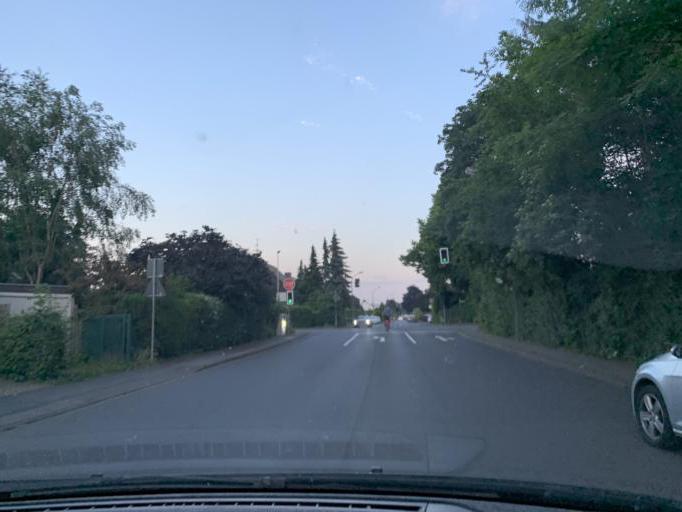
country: DE
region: North Rhine-Westphalia
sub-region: Regierungsbezirk Koln
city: Pulheim
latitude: 51.0017
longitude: 6.8140
